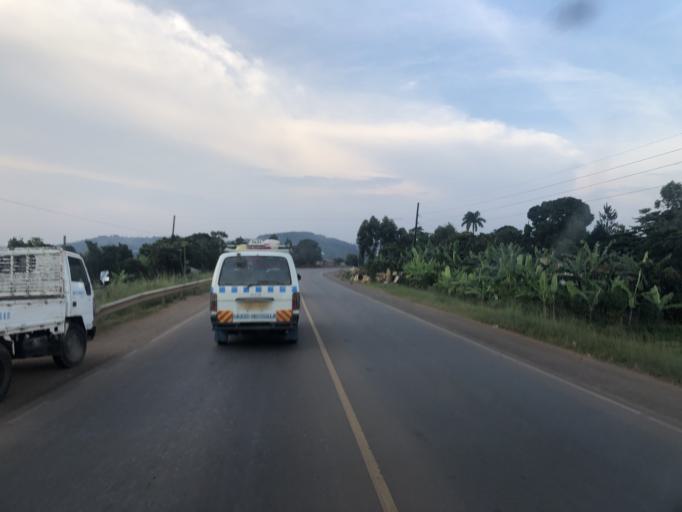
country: UG
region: Central Region
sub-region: Mpigi District
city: Mpigi
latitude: 0.2378
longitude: 32.3484
